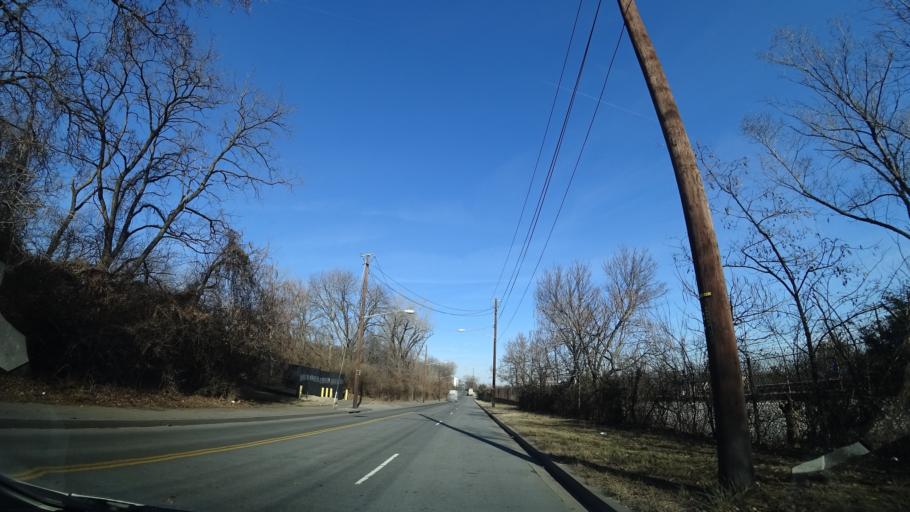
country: US
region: Maryland
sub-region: Prince George's County
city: Chillum
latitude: 38.9439
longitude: -76.9992
